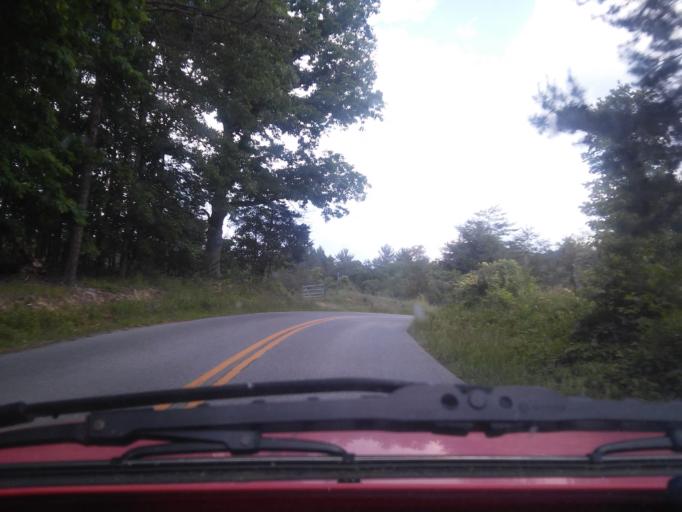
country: US
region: Virginia
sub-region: Craig County
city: New Castle
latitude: 37.5750
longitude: -80.0222
